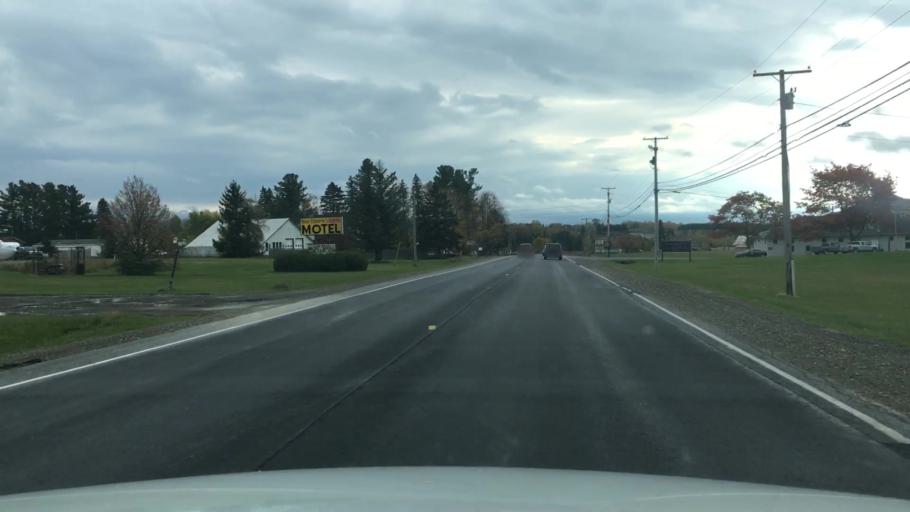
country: US
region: Maine
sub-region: Aroostook County
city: Presque Isle
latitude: 46.6551
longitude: -68.0055
